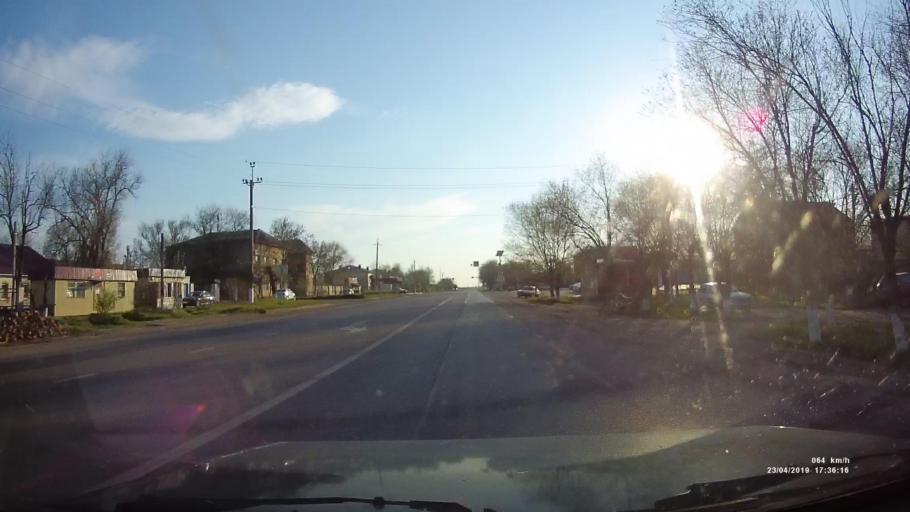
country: RU
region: Kalmykiya
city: Priyutnoye
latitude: 46.0966
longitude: 43.5085
